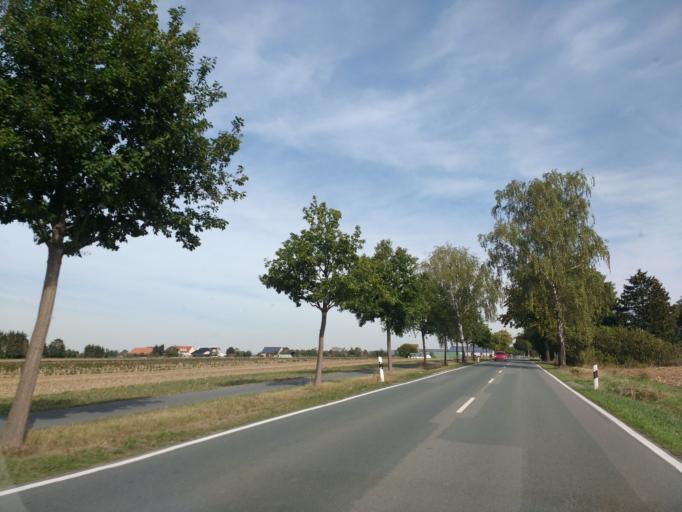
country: DE
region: North Rhine-Westphalia
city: Bad Lippspringe
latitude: 51.7728
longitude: 8.8394
